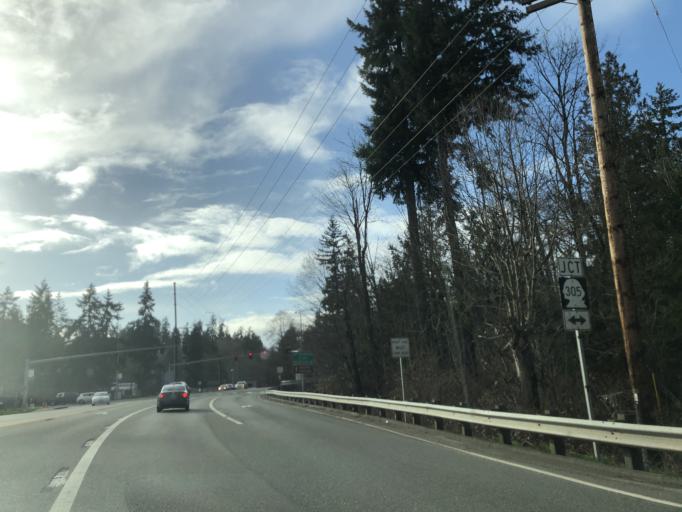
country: US
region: Washington
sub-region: Kitsap County
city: Poulsbo
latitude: 47.7524
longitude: -122.6446
